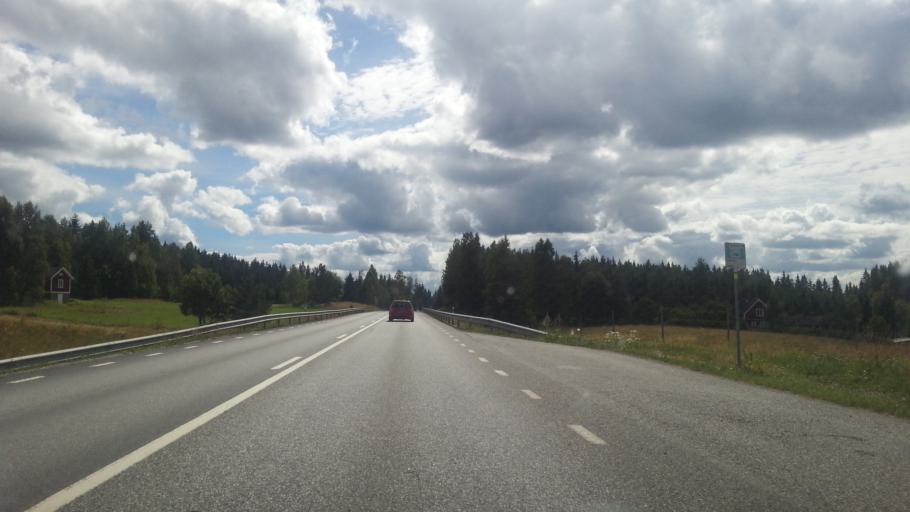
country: SE
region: OErebro
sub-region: Lindesbergs Kommun
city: Stora
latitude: 59.8142
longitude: 15.1389
